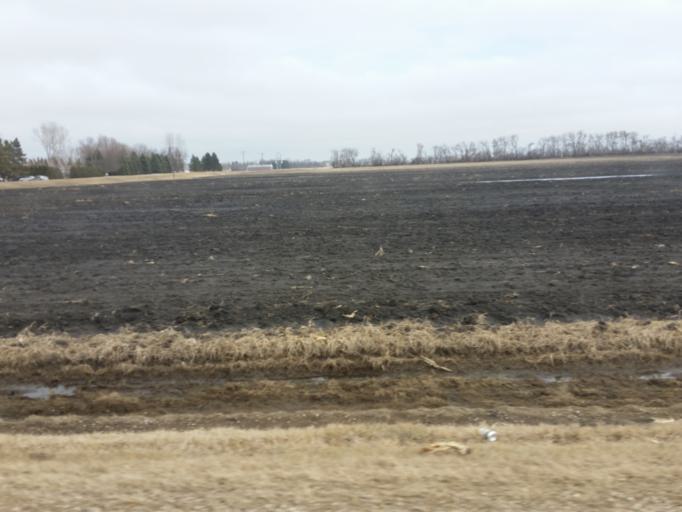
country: US
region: North Dakota
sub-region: Walsh County
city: Grafton
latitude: 48.4262
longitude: -97.3212
